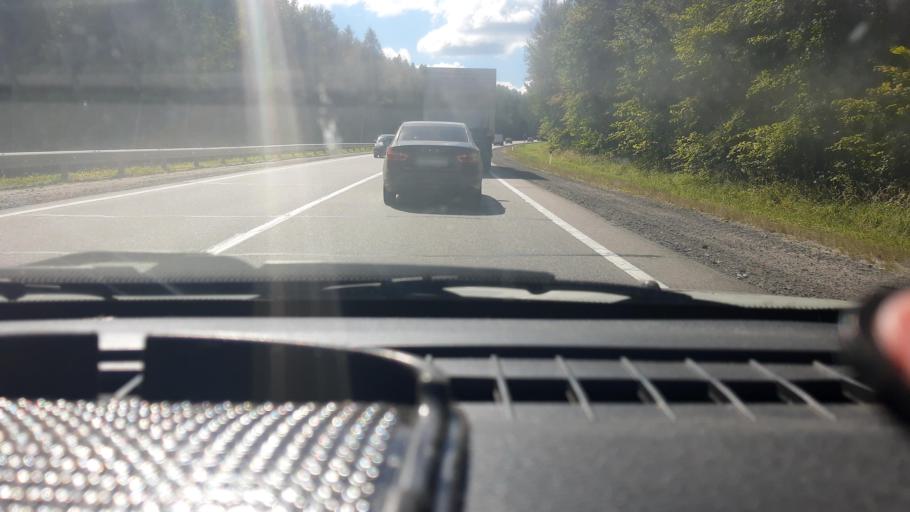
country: RU
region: Nizjnij Novgorod
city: Surovatikha
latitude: 55.5968
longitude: 43.9863
